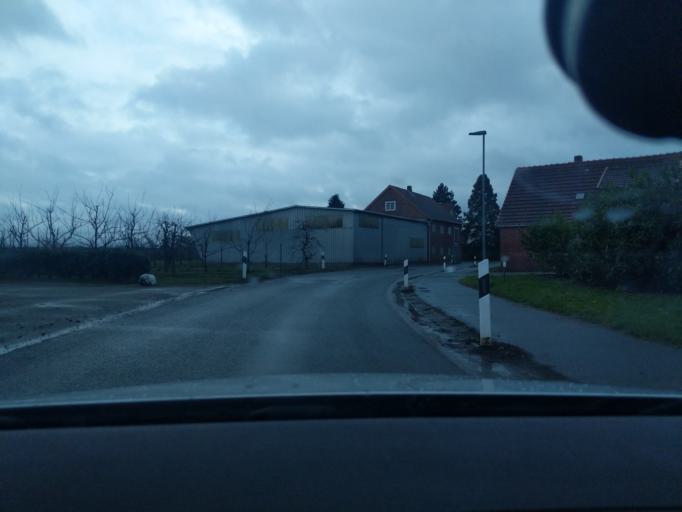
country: DE
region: Lower Saxony
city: Mittelnkirchen
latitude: 53.5279
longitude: 9.6464
